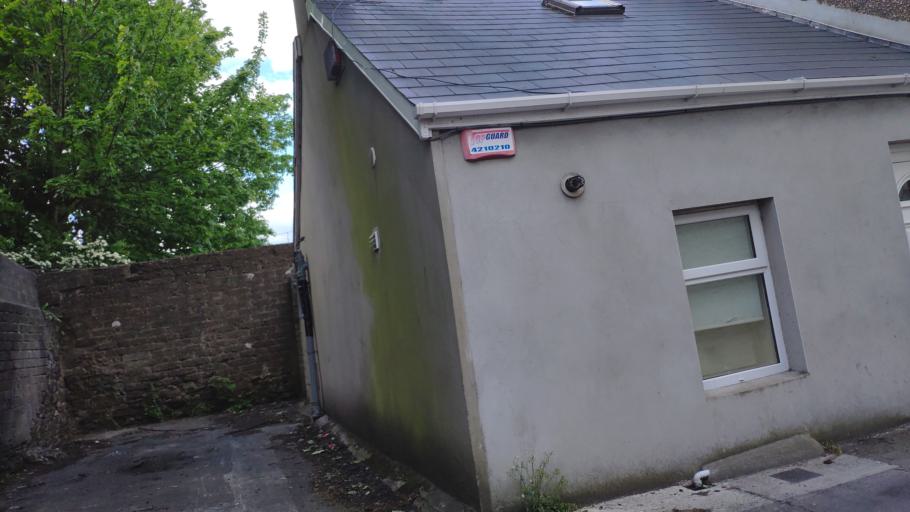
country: IE
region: Munster
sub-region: County Cork
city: Cork
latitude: 51.9096
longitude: -8.4553
